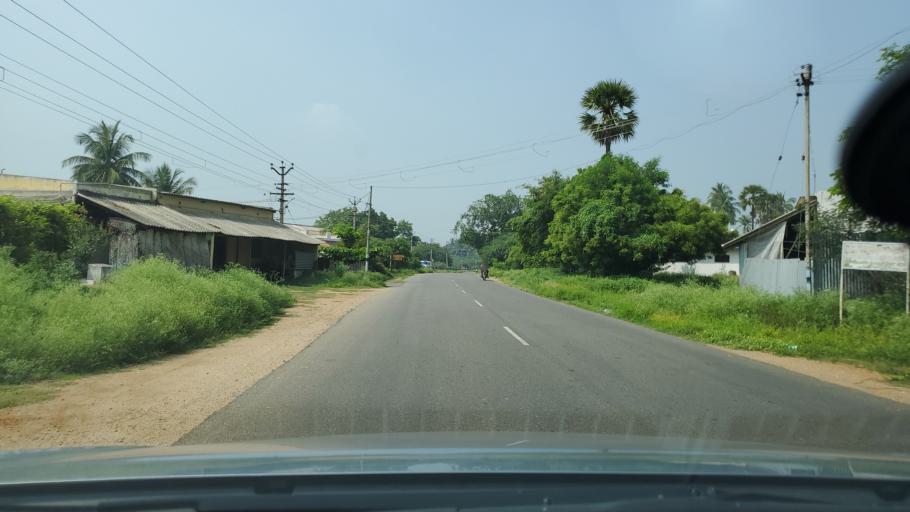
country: IN
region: Tamil Nadu
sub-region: Erode
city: Chennimalai
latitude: 11.1905
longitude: 77.6202
